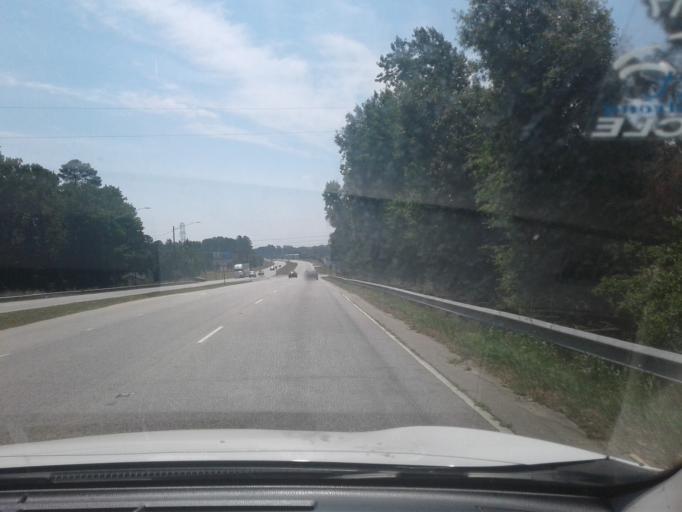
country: US
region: North Carolina
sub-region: Harnett County
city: Erwin
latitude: 35.3292
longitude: -78.6620
